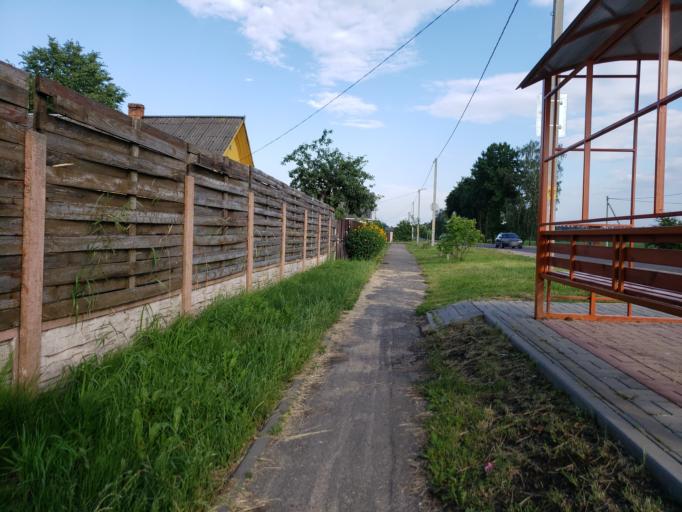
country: BY
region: Minsk
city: Chervyen'
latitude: 53.7009
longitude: 28.4451
